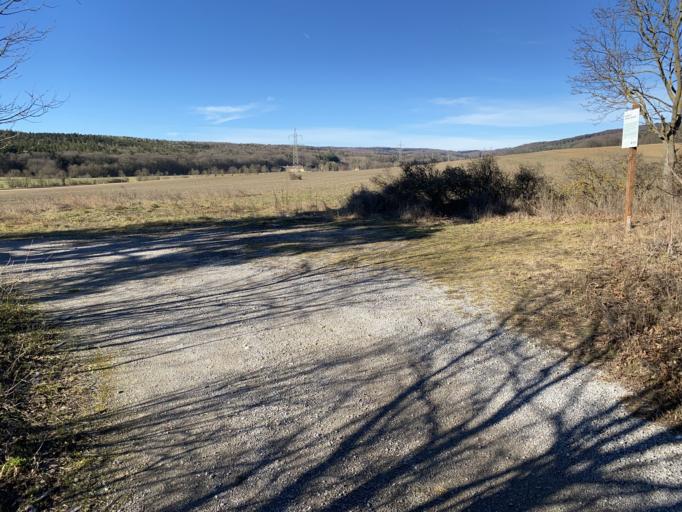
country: AT
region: Lower Austria
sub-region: Politischer Bezirk Baden
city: Hirtenberg
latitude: 47.9670
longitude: 16.1583
